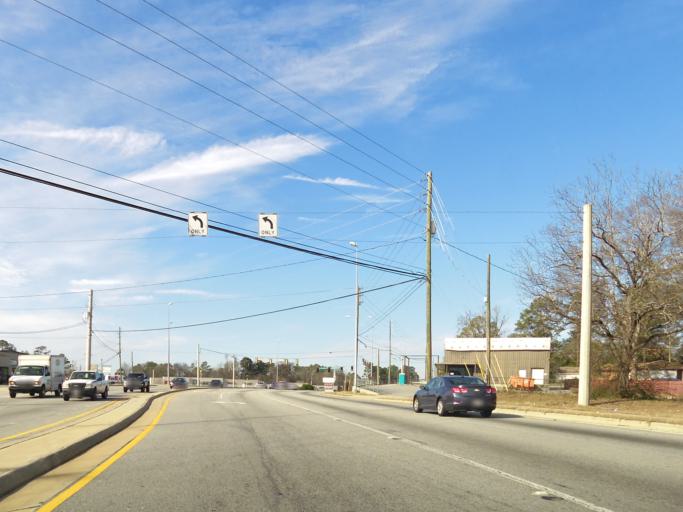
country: US
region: Georgia
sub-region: Bibb County
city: Macon
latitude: 32.8258
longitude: -83.7114
